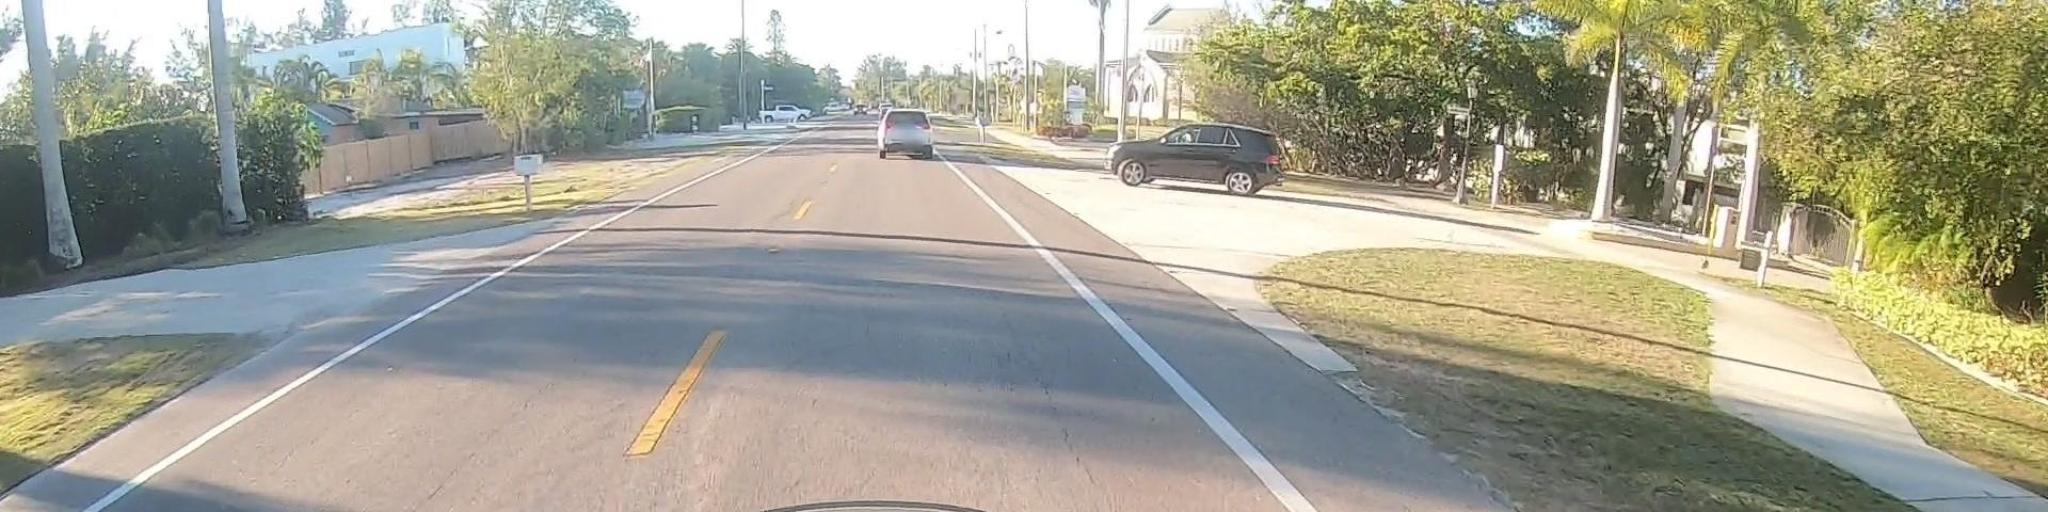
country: US
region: Florida
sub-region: Manatee County
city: Longboat Key
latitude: 27.4247
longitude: -82.6730
